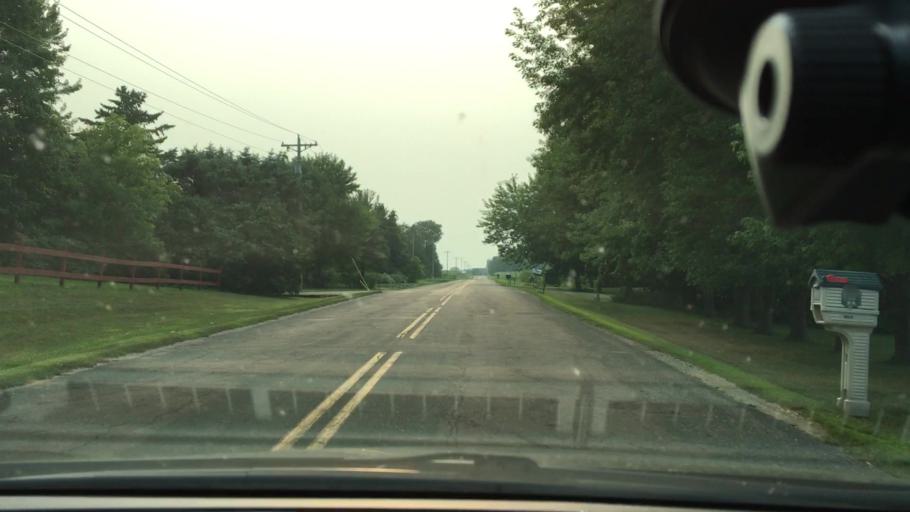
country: US
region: Minnesota
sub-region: Wright County
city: Albertville
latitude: 45.2666
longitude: -93.6734
